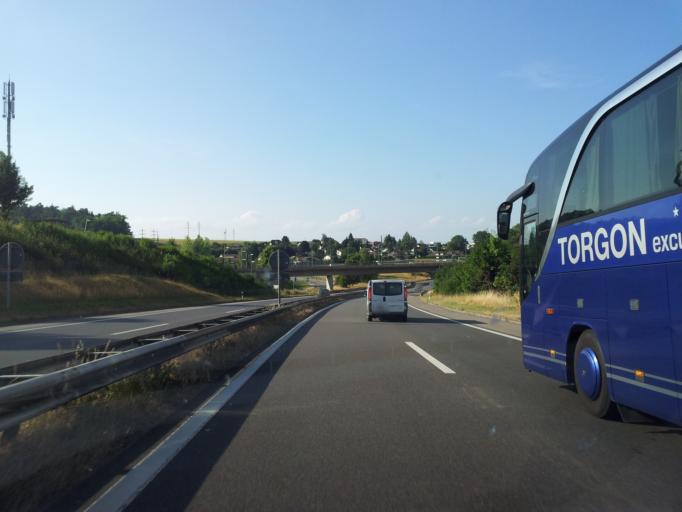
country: CH
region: Fribourg
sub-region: Sarine District
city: Givisiez
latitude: 46.8160
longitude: 7.1377
